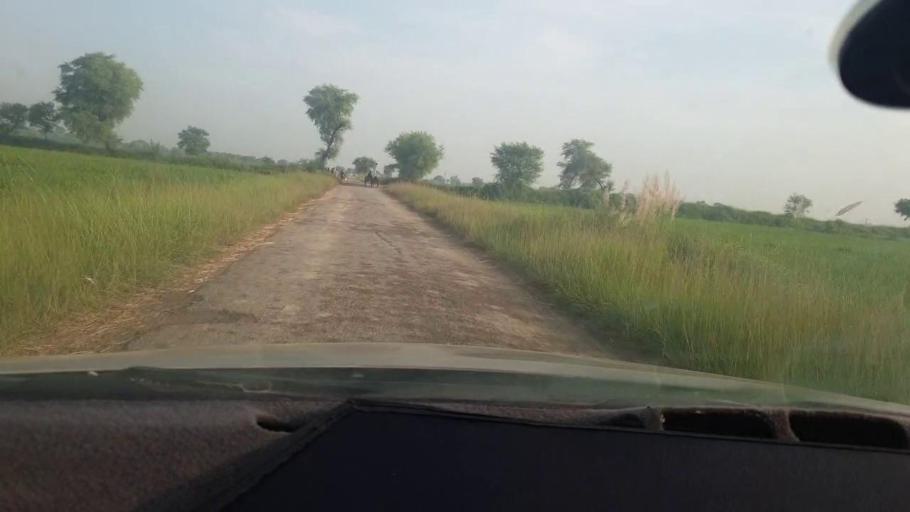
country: PK
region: Sindh
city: Jacobabad
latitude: 28.3021
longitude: 68.4150
